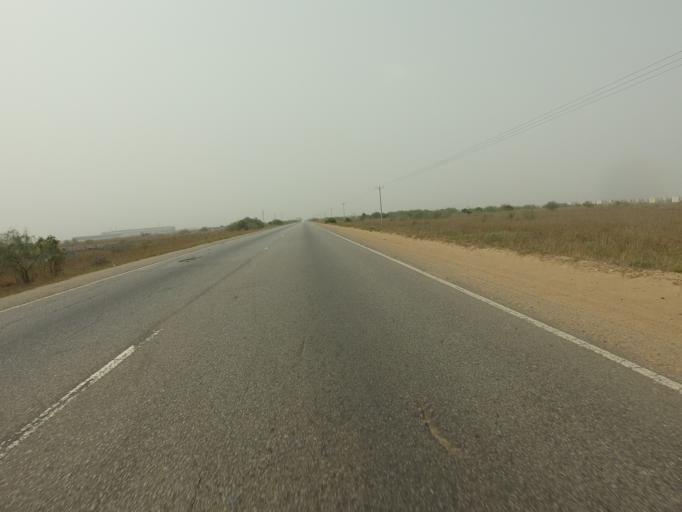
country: GH
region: Greater Accra
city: Tema
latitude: 5.8297
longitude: 0.2056
